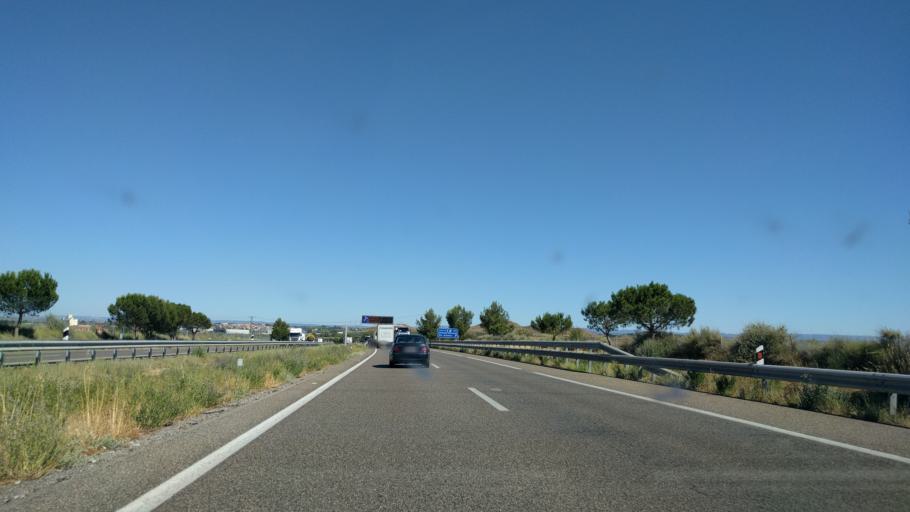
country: ES
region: Catalonia
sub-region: Provincia de Lleida
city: Alcoletge
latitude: 41.6327
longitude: 0.6933
